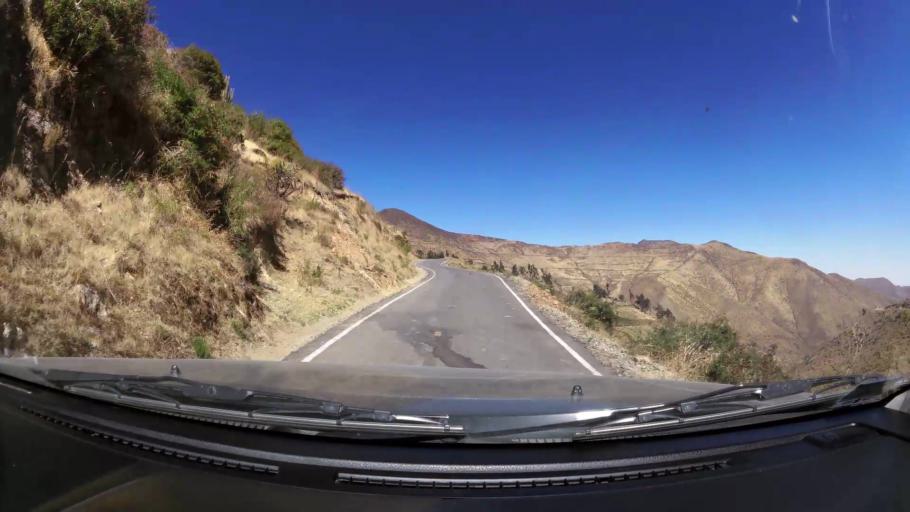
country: PE
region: Huancavelica
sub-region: Huaytara
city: Quito-Arma
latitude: -13.6815
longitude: -75.3803
